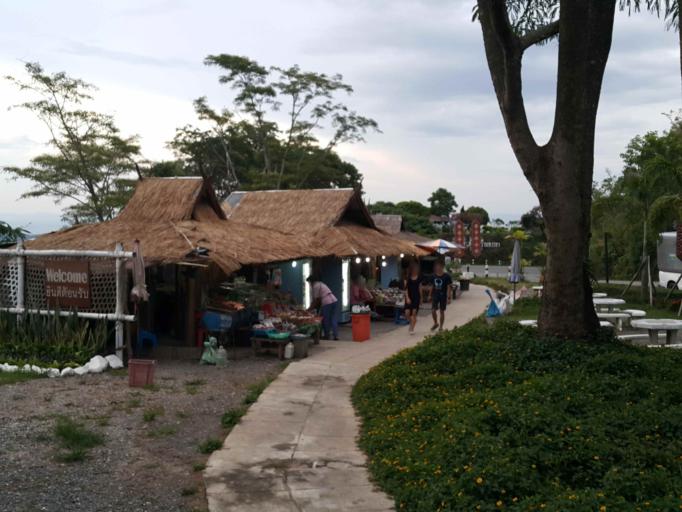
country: TH
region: Phayao
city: Phayao
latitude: 19.0614
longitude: 99.7808
